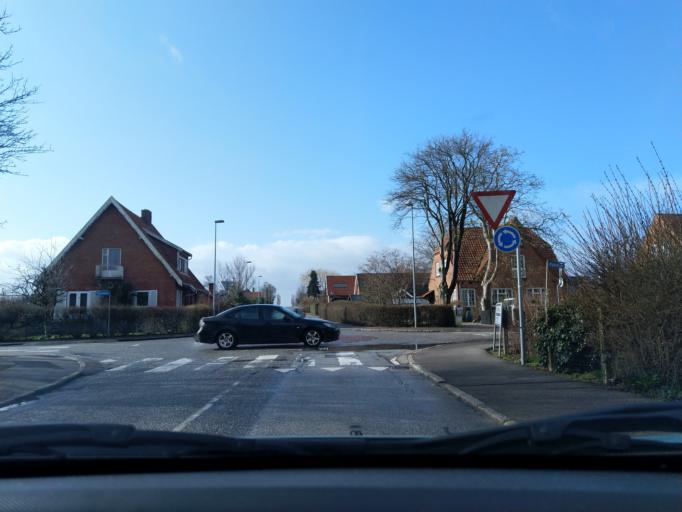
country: DK
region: Zealand
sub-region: Naestved Kommune
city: Naestved
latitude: 55.2207
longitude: 11.7647
